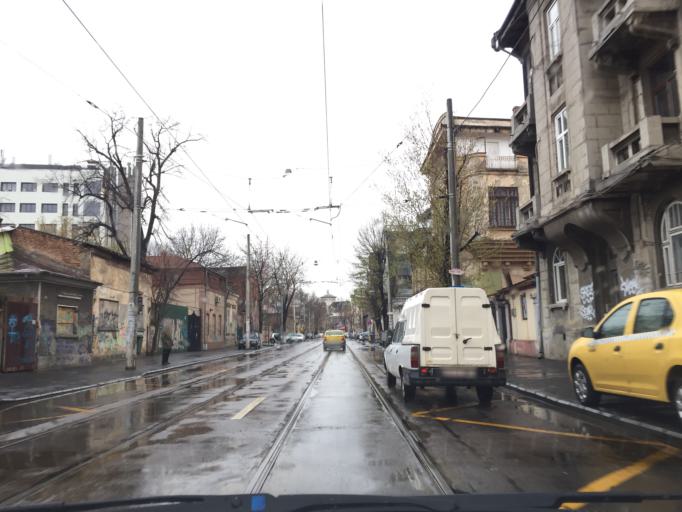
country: RO
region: Bucuresti
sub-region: Municipiul Bucuresti
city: Bucuresti
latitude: 44.4195
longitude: 26.0950
